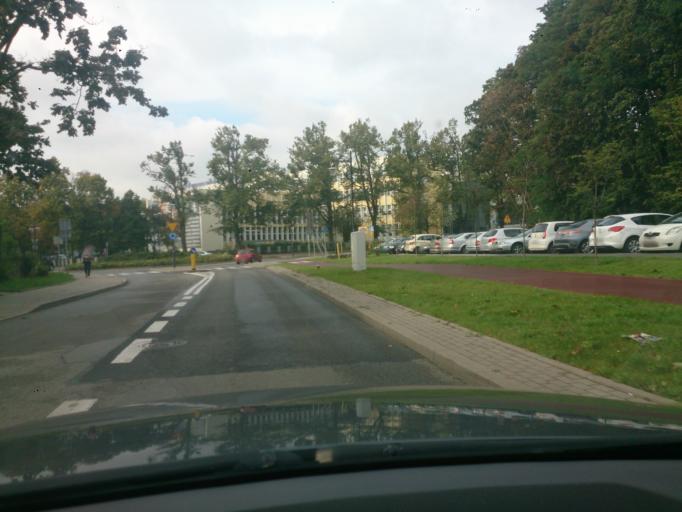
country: PL
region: Pomeranian Voivodeship
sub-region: Sopot
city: Sopot
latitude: 54.4461
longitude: 18.5562
